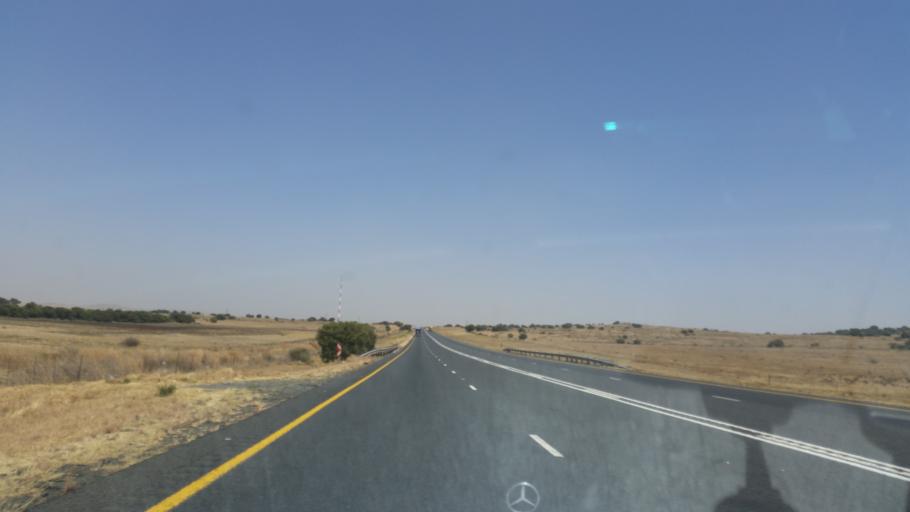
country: ZA
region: Orange Free State
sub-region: Lejweleputswa District Municipality
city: Winburg
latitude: -28.7102
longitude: 26.7845
